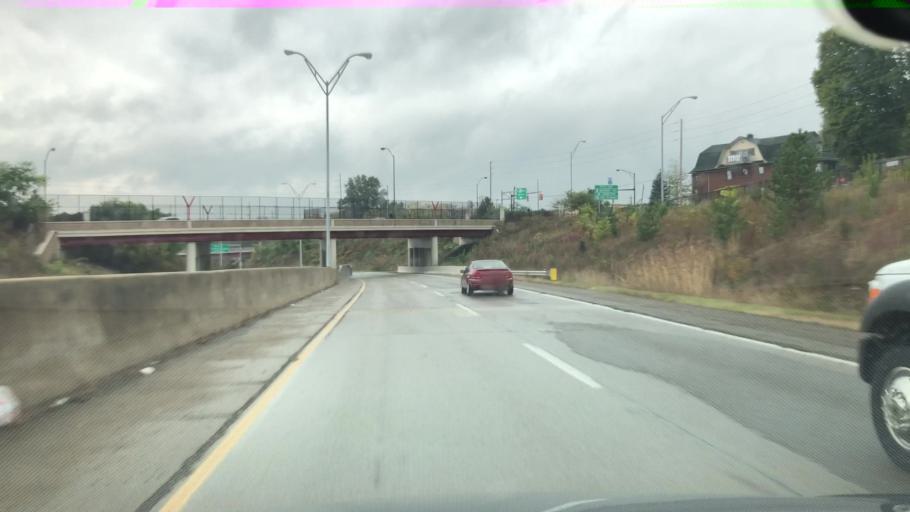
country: US
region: Ohio
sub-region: Mahoning County
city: Youngstown
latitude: 41.1111
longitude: -80.6500
